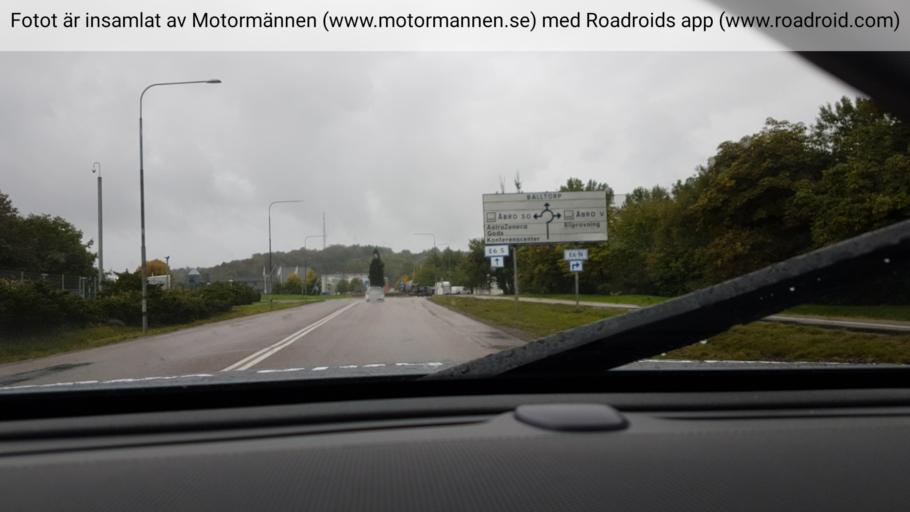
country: SE
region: Vaestra Goetaland
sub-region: Molndal
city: Moelndal
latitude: 57.6433
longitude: 12.0178
